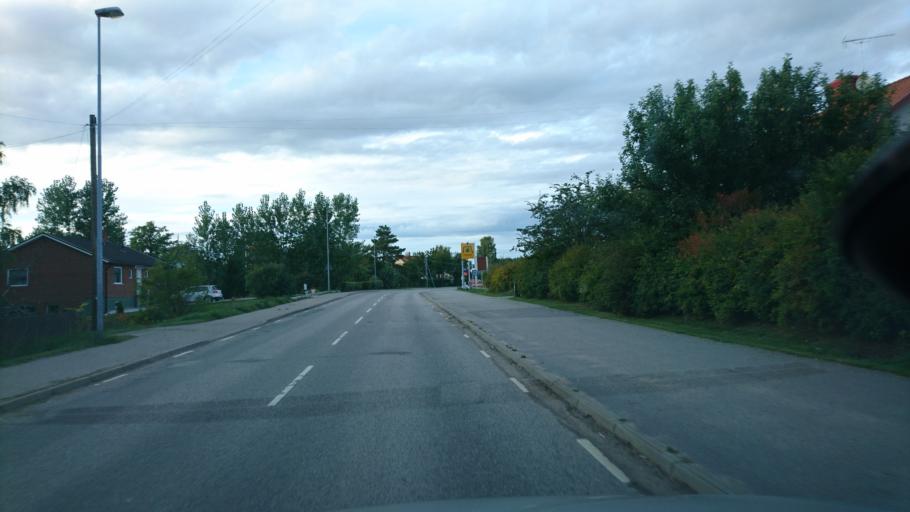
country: SE
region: Soedermanland
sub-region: Strangnas Kommun
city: Stallarholmen
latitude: 59.3618
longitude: 17.2053
